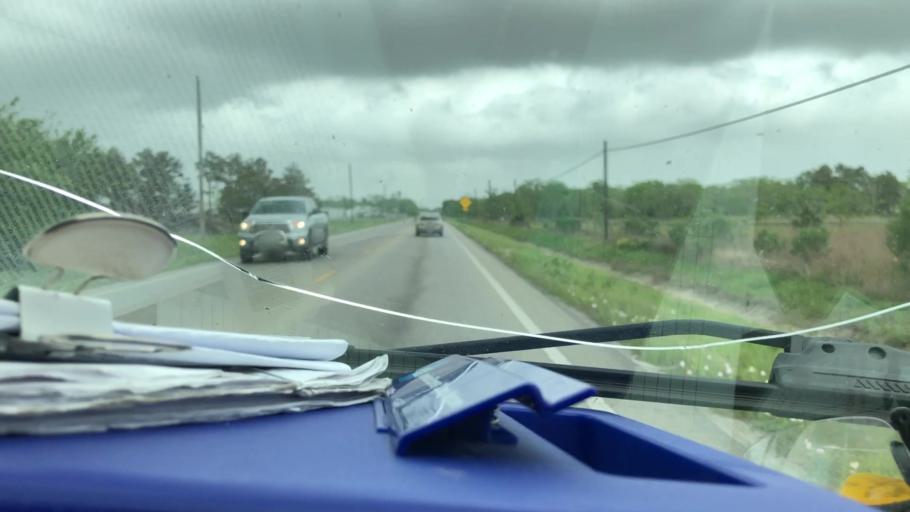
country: US
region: Texas
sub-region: Galveston County
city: Bacliff
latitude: 29.4786
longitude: -94.9706
